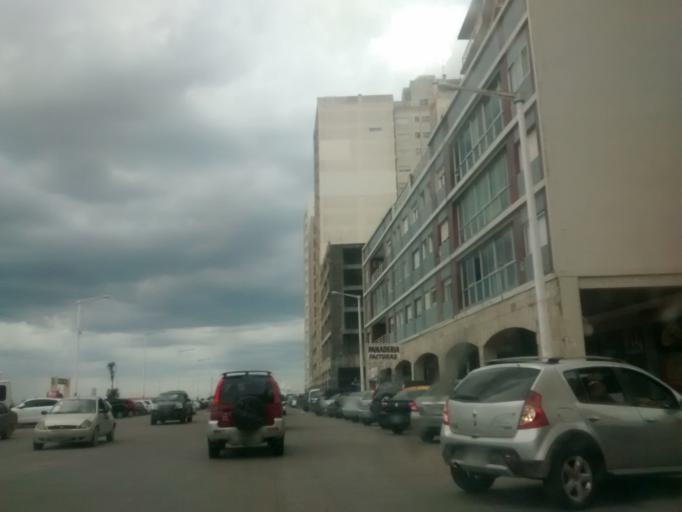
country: AR
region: Buenos Aires
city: Necochea
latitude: -38.5843
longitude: -58.7318
